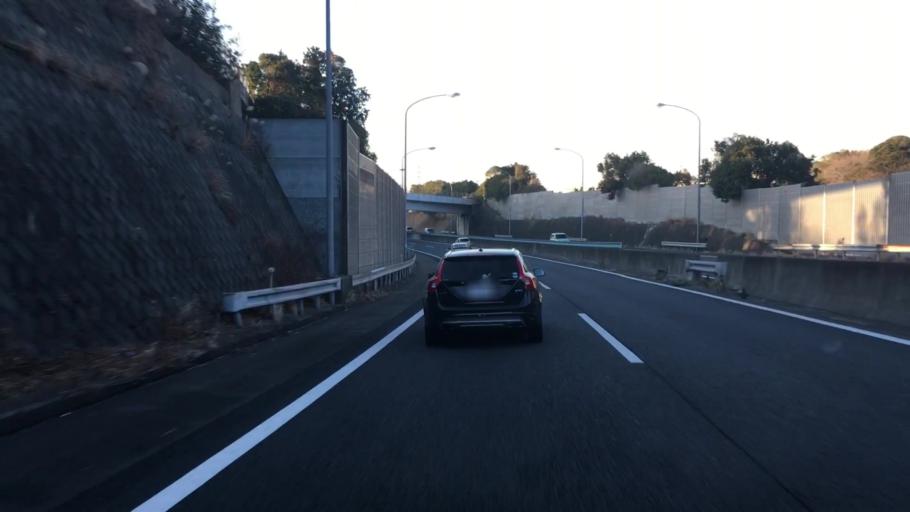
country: JP
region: Kanagawa
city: Kamakura
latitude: 35.3707
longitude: 139.5937
